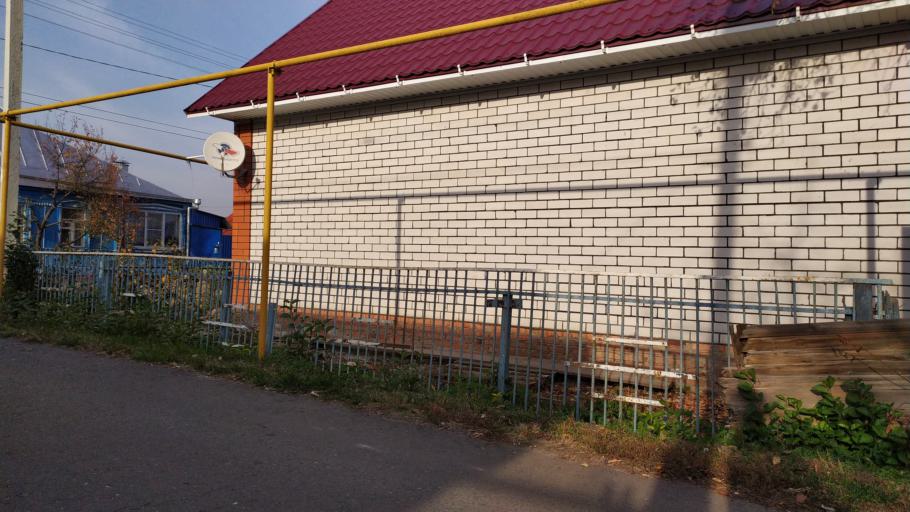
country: RU
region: Kursk
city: Kursk
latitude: 51.6435
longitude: 36.1479
